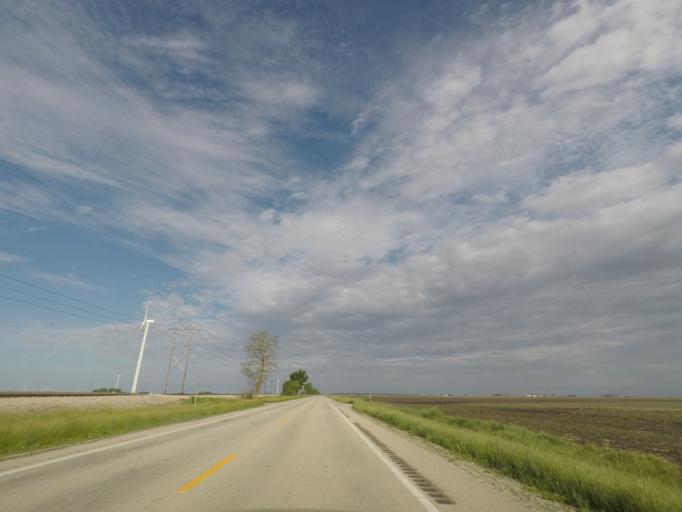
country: US
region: Illinois
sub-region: Logan County
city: Mount Pulaski
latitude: 39.9866
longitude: -89.2275
